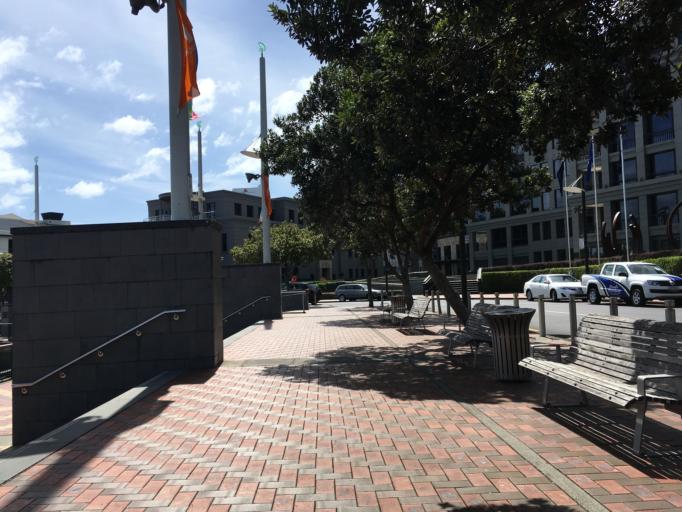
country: NZ
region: Auckland
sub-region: Auckland
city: Auckland
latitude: -36.8452
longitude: 174.7583
